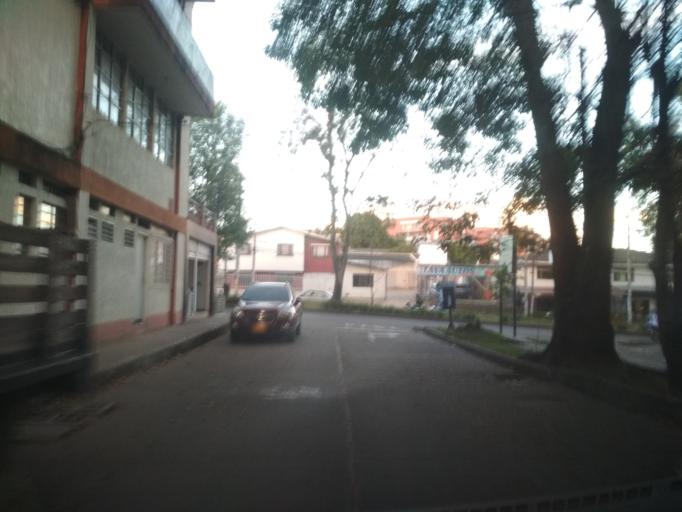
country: CO
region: Cauca
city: Popayan
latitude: 2.4495
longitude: -76.6063
